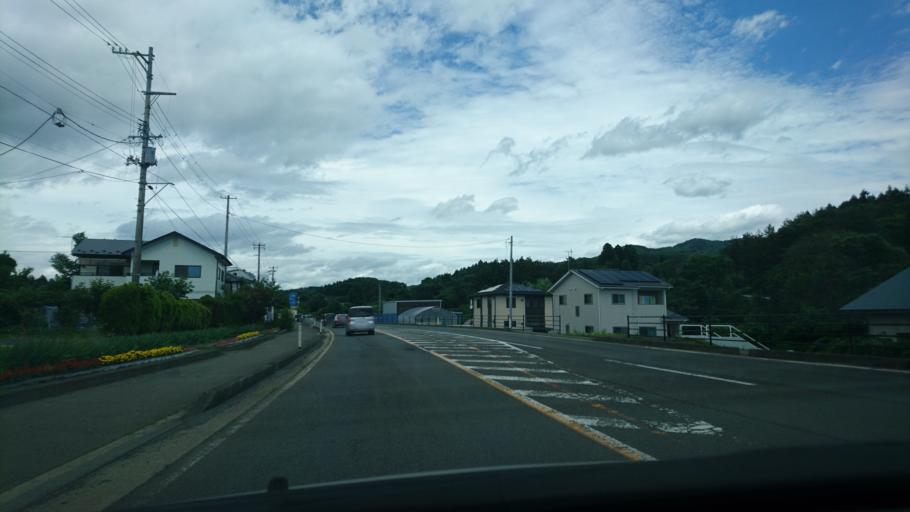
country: JP
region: Iwate
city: Morioka-shi
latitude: 39.6076
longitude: 141.2037
